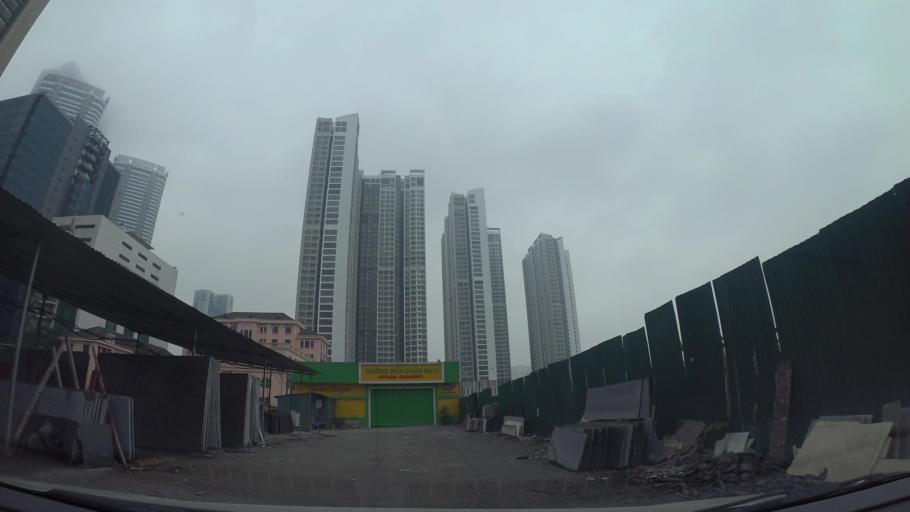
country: VN
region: Ha Noi
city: Cau Giay
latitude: 21.0213
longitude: 105.7843
